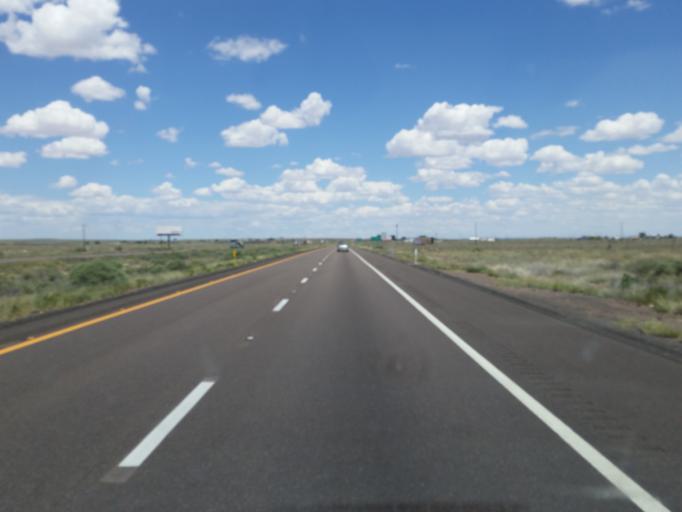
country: US
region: Arizona
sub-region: Navajo County
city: Holbrook
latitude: 34.9776
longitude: -110.0711
